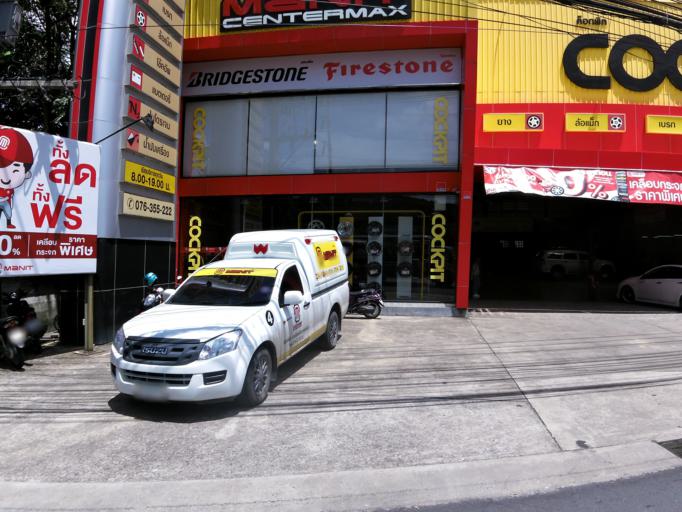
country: TH
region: Phuket
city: Mueang Phuket
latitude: 7.8740
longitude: 98.3634
